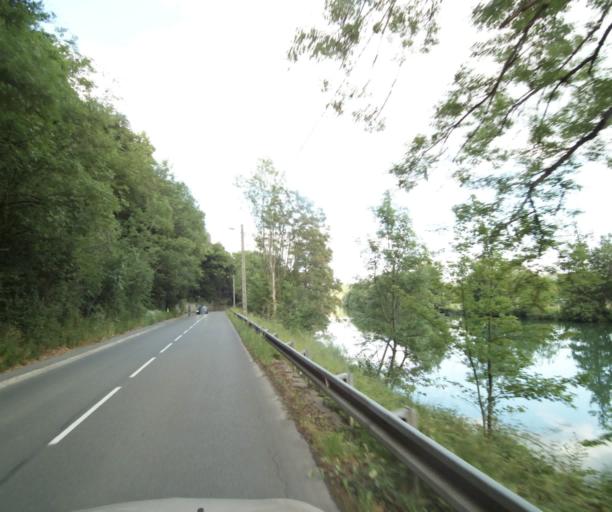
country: FR
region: Champagne-Ardenne
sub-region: Departement des Ardennes
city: Charleville-Mezieres
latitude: 49.7844
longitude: 4.7224
